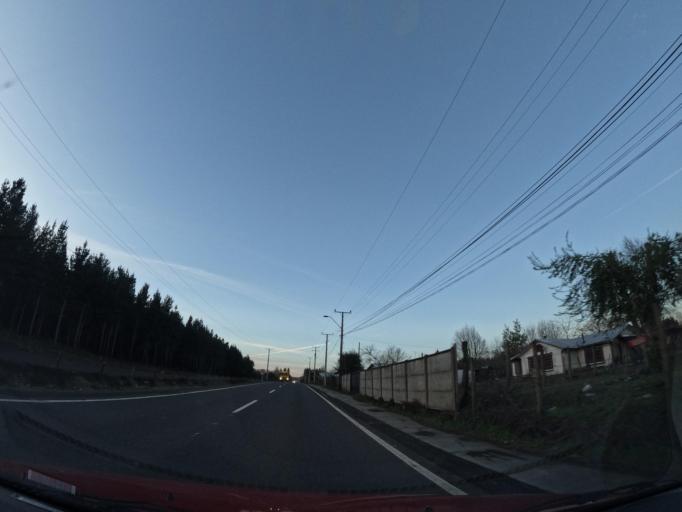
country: CL
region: Biobio
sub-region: Provincia de Biobio
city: Los Angeles
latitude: -37.3897
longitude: -72.0098
